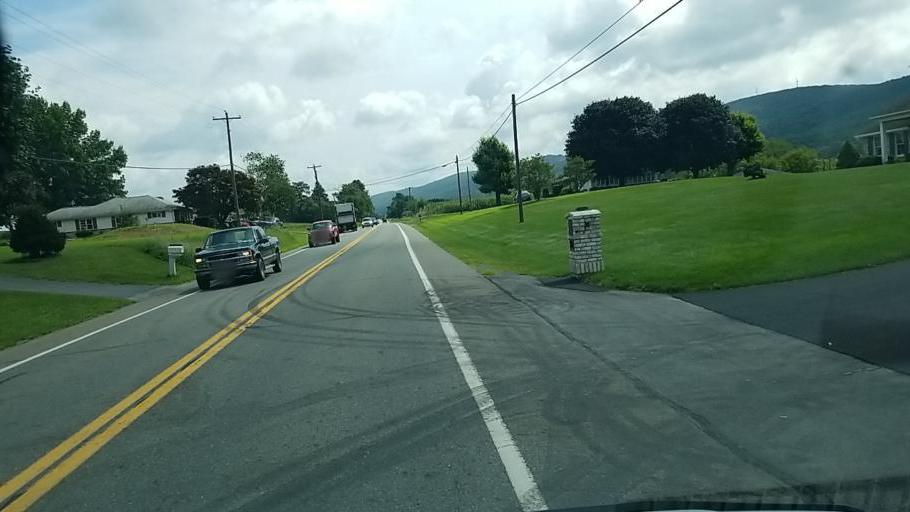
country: US
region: Pennsylvania
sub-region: Dauphin County
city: Elizabethville
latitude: 40.5454
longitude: -76.8511
